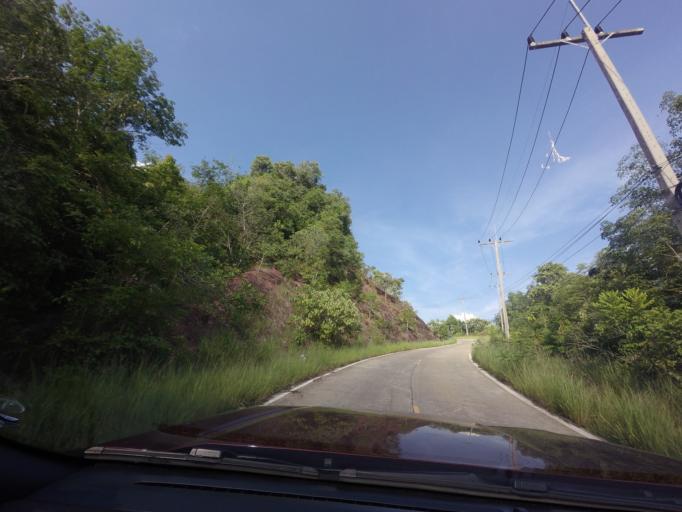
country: TH
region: Yala
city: Than To
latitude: 6.0988
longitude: 101.3100
